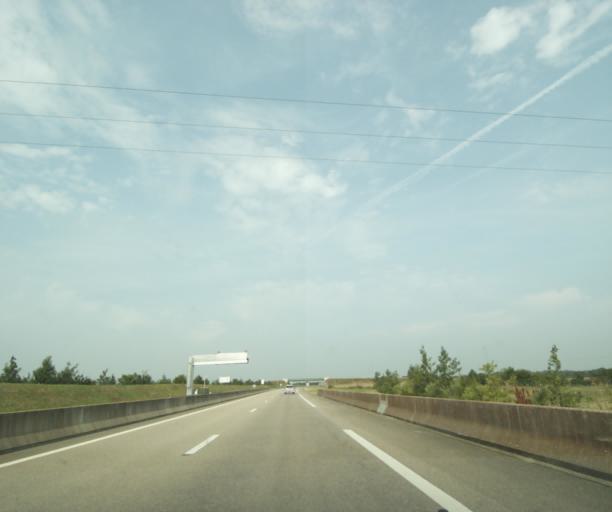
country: FR
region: Lower Normandy
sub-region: Departement du Calvados
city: Falaise
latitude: 48.8717
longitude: -0.2108
